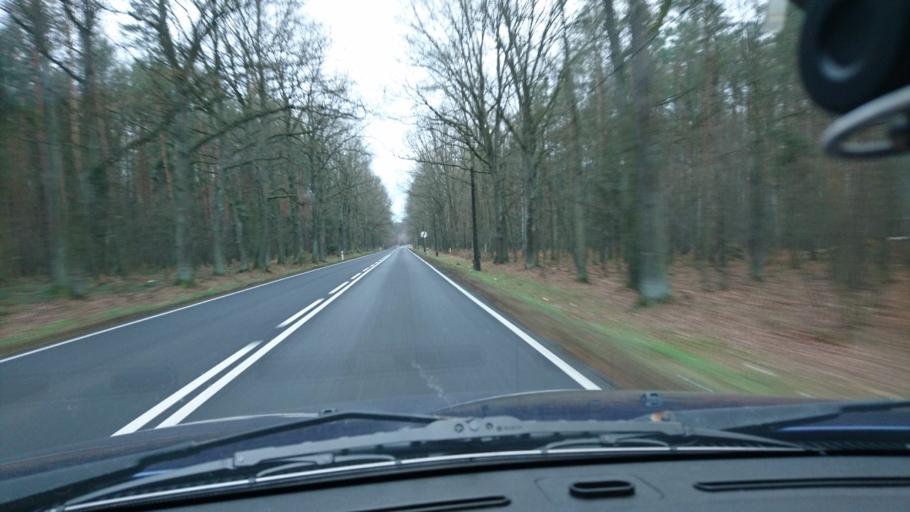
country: PL
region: Opole Voivodeship
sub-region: Powiat kluczborski
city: Kluczbork
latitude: 50.9496
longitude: 18.3135
